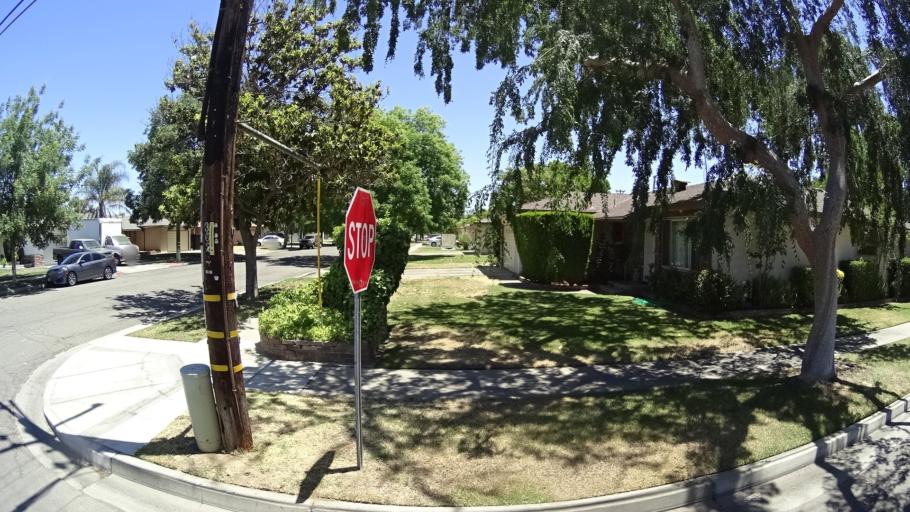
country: US
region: California
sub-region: Fresno County
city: Tarpey Village
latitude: 36.7965
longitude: -119.7532
